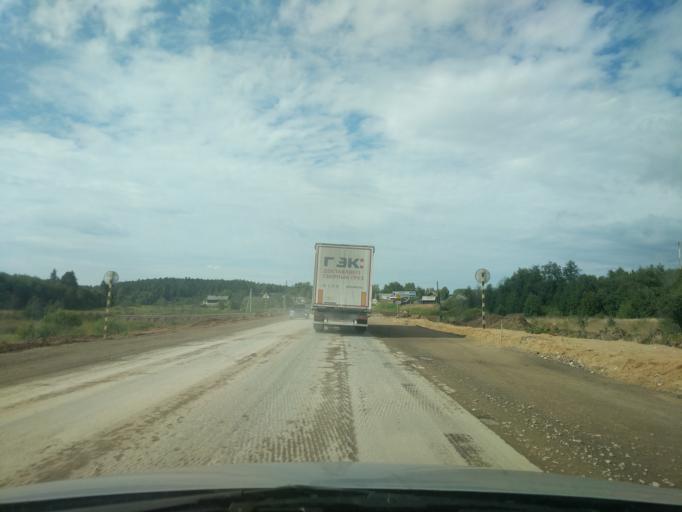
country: RU
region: Kostroma
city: Sudislavl'
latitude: 57.8754
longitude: 41.7332
